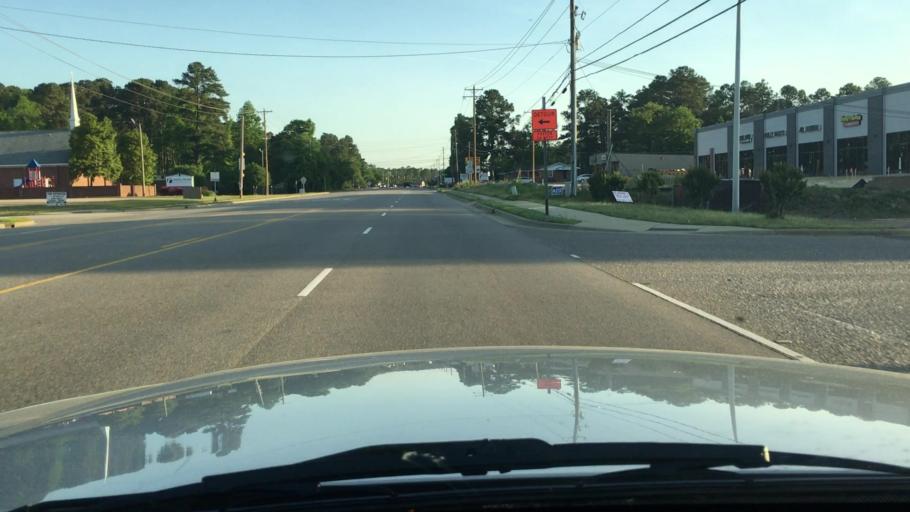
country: US
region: North Carolina
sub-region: Cumberland County
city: Fort Bragg
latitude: 35.0946
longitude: -79.0109
